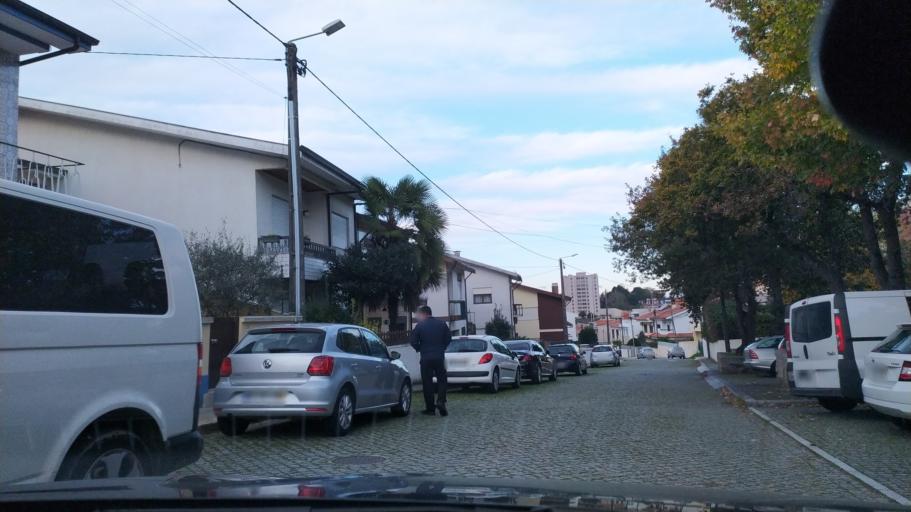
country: PT
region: Porto
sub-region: Maia
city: Maia
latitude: 41.2449
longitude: -8.6408
